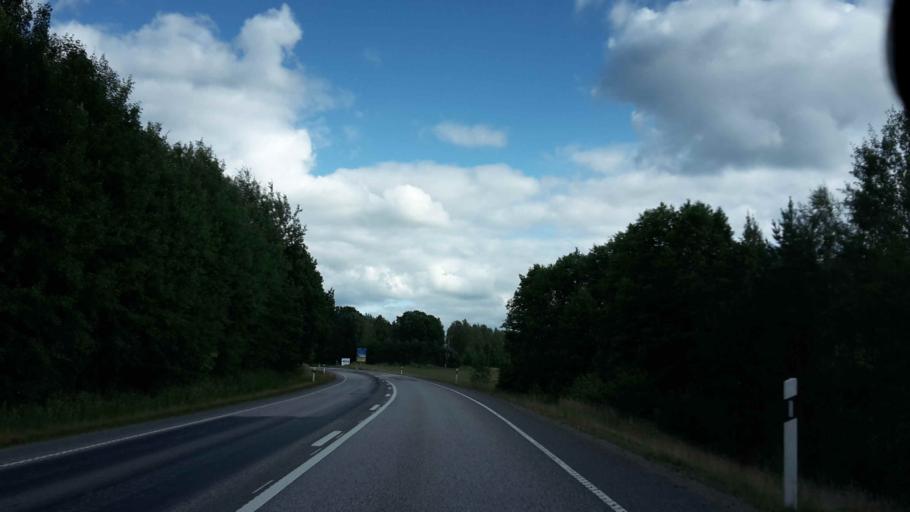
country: SE
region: OEstergoetland
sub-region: Linkopings Kommun
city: Ljungsbro
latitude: 58.7833
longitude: 15.5025
